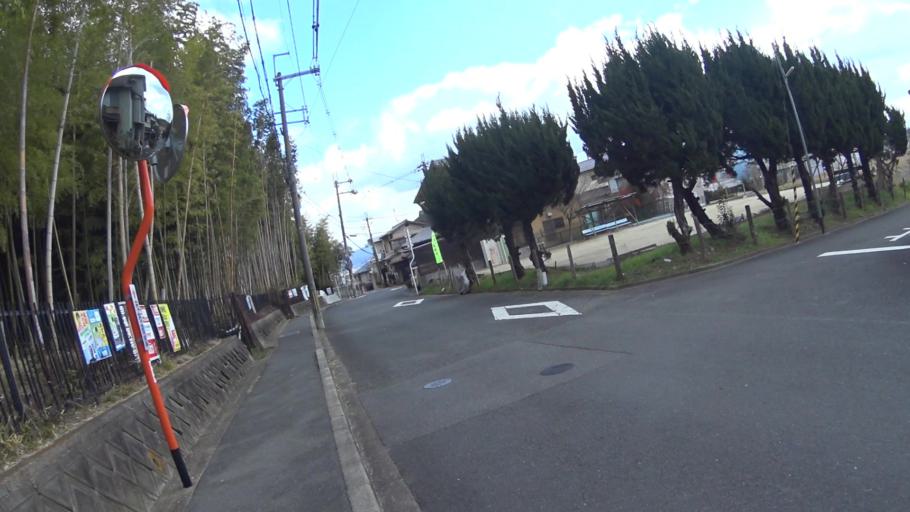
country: JP
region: Kyoto
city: Muko
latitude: 34.9533
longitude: 135.6946
